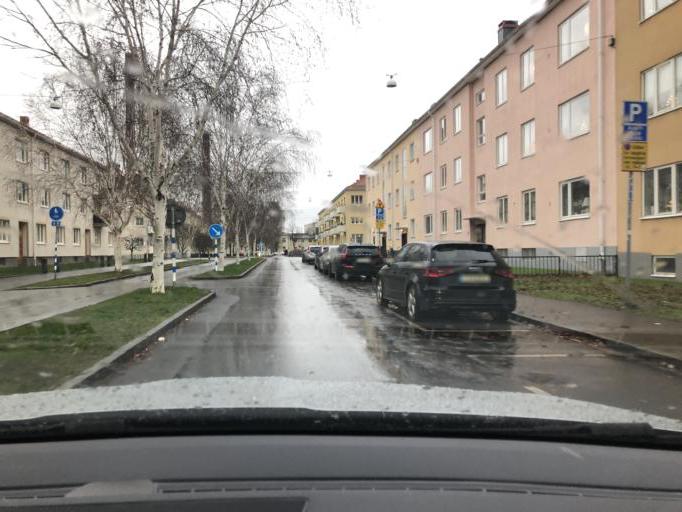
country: SE
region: Joenkoeping
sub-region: Jonkopings Kommun
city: Jonkoping
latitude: 57.7754
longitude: 14.1549
